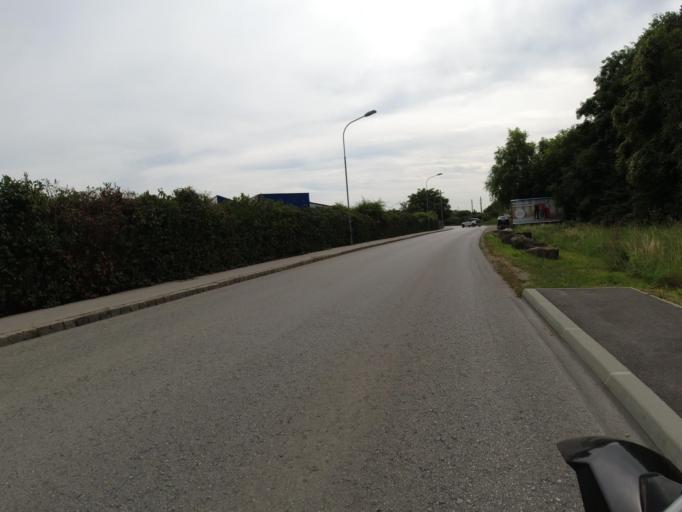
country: AT
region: Lower Austria
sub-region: Politischer Bezirk Modling
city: Wiener Neudorf
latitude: 48.0762
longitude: 16.3030
